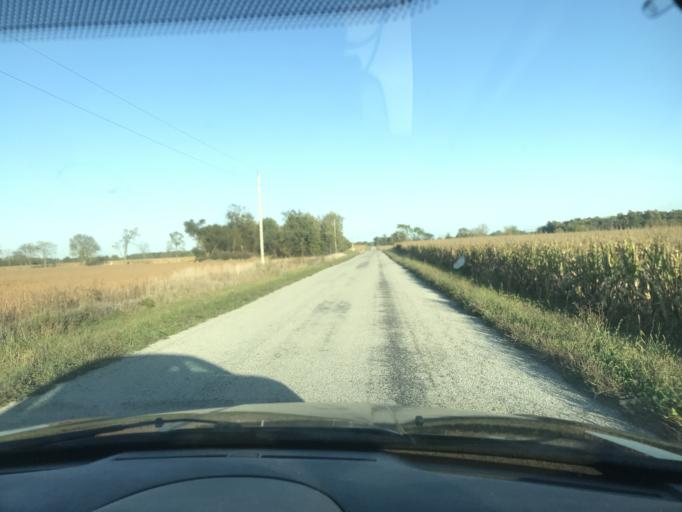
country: US
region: Ohio
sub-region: Logan County
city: West Liberty
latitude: 40.2337
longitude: -83.8371
